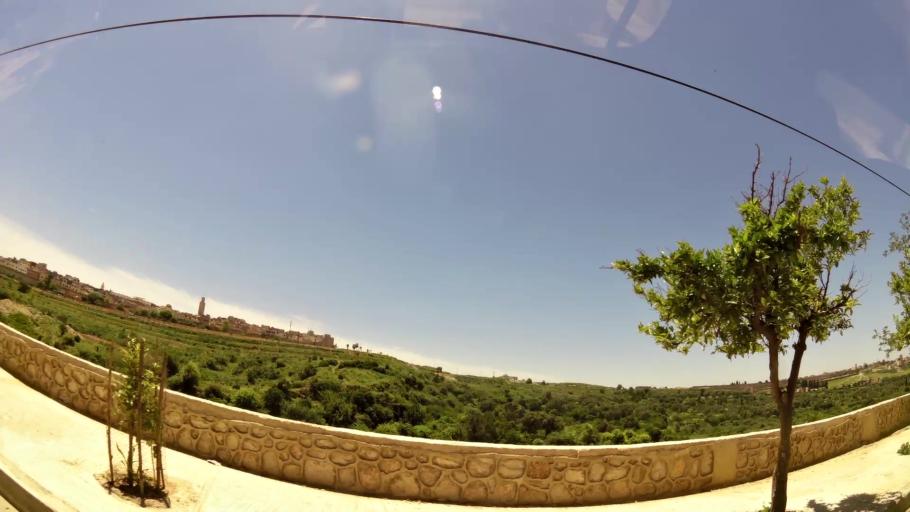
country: MA
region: Meknes-Tafilalet
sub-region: Meknes
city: Meknes
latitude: 33.9038
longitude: -5.5641
